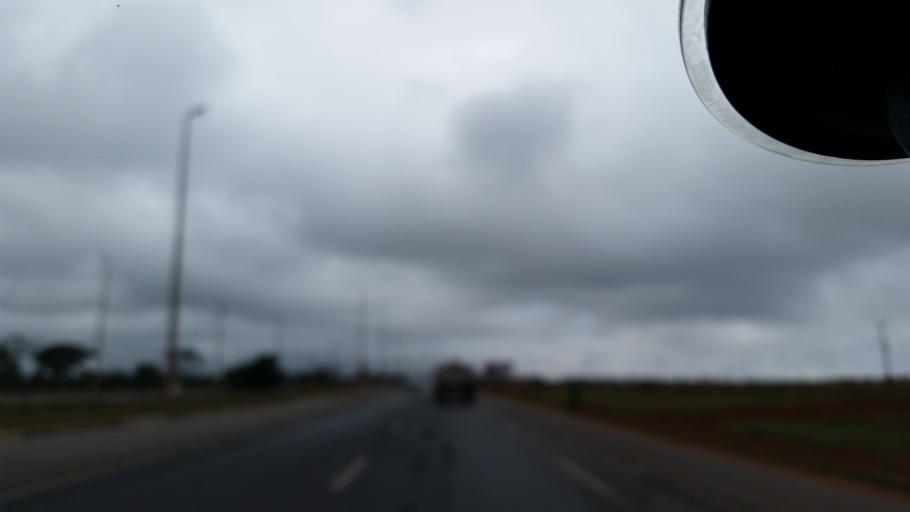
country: BR
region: Federal District
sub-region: Brasilia
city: Brasilia
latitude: -15.9676
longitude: -47.9919
